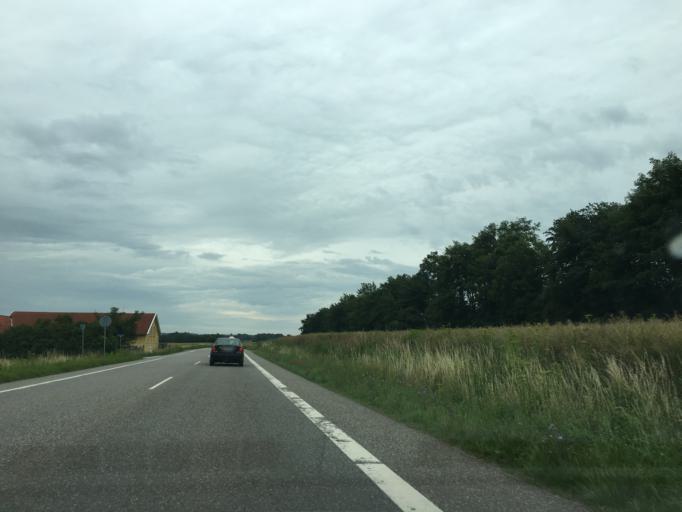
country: DK
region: Zealand
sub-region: Kalundborg Kommune
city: Svebolle
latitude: 55.6658
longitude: 11.2403
